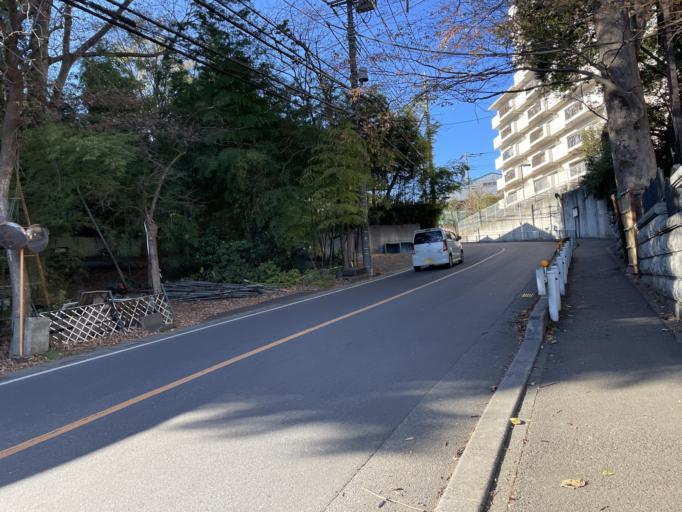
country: JP
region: Saitama
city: Asaka
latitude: 35.8044
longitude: 139.5814
